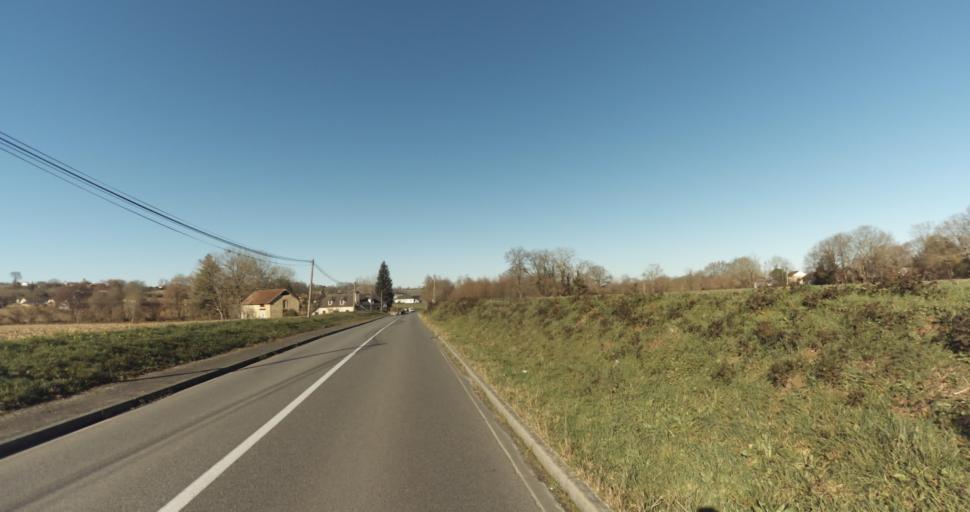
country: FR
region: Aquitaine
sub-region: Departement des Pyrenees-Atlantiques
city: Morlaas
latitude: 43.3530
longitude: -0.2671
